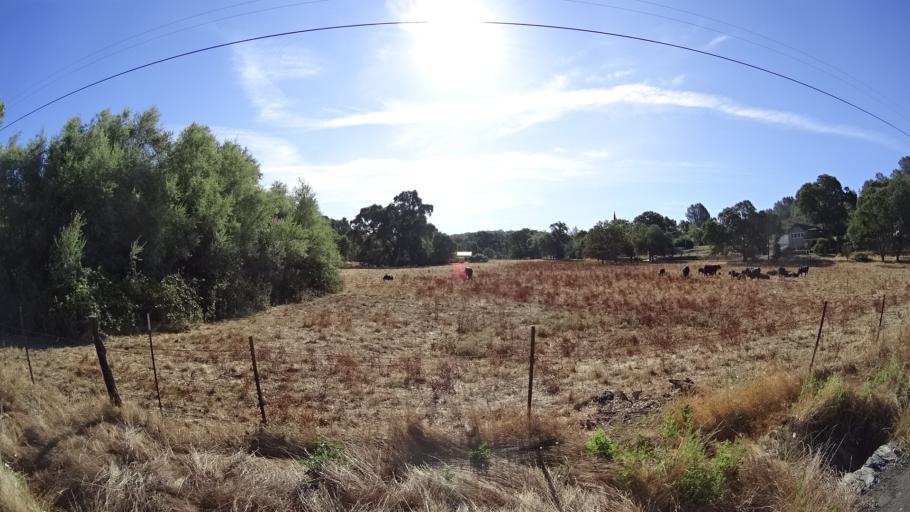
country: US
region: California
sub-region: Calaveras County
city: Valley Springs
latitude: 38.2101
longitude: -120.7862
